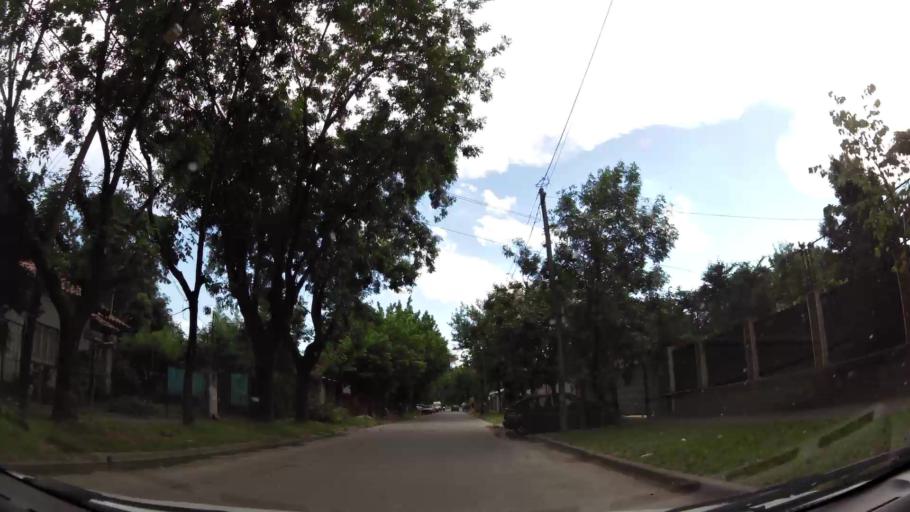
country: AR
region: Buenos Aires
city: Ituzaingo
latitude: -34.6337
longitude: -58.6952
